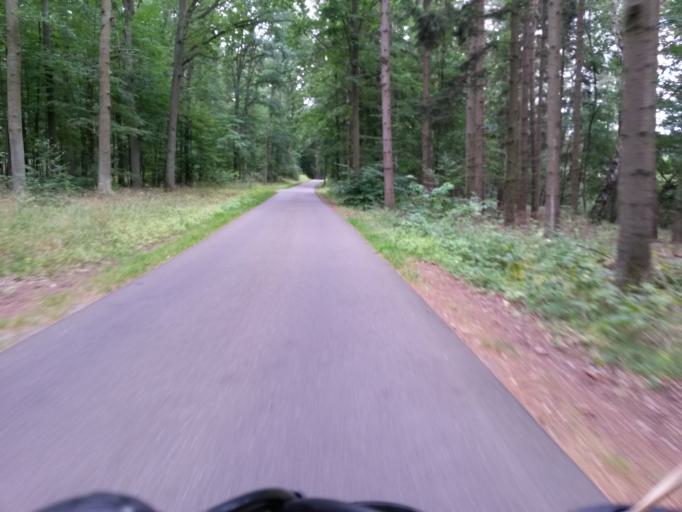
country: DE
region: Brandenburg
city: Angermunde
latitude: 53.0618
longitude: 13.9338
